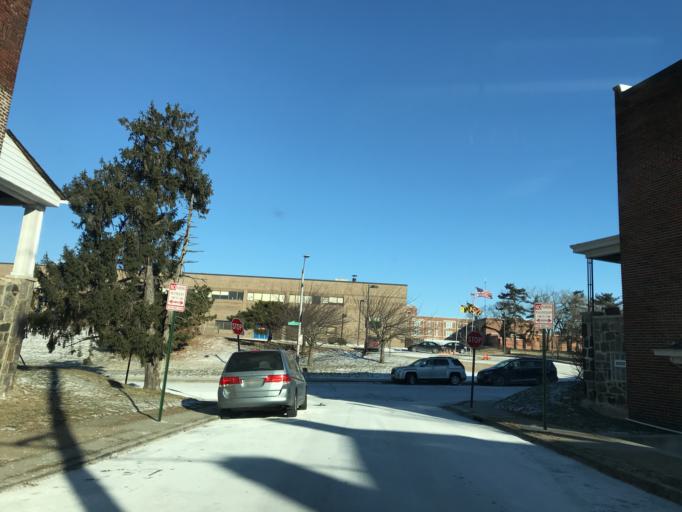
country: US
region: Maryland
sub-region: City of Baltimore
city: Baltimore
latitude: 39.3119
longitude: -76.6549
